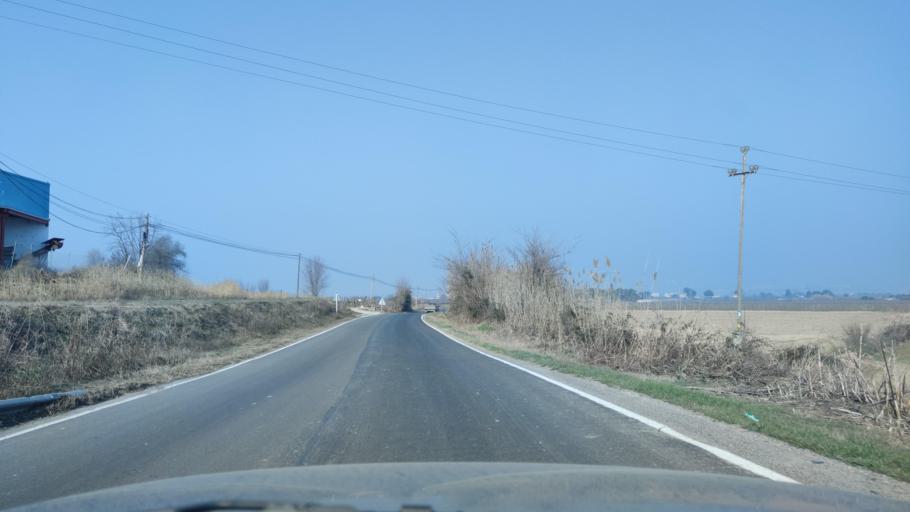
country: ES
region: Catalonia
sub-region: Provincia de Lleida
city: Alfes
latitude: 41.5611
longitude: 0.6147
